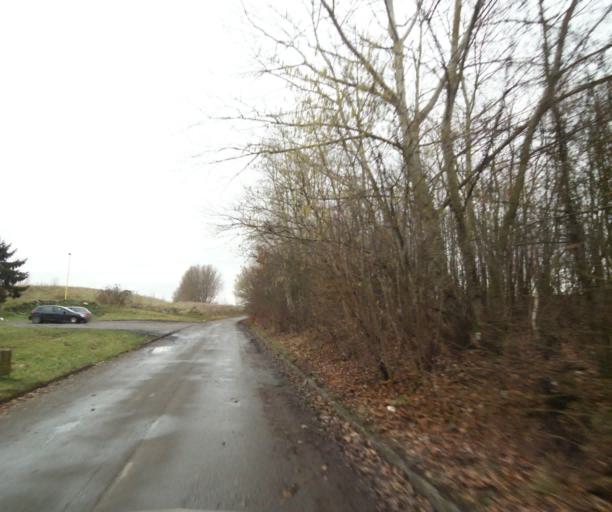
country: FR
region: Nord-Pas-de-Calais
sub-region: Departement du Nord
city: Escautpont
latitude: 50.4074
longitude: 3.5636
